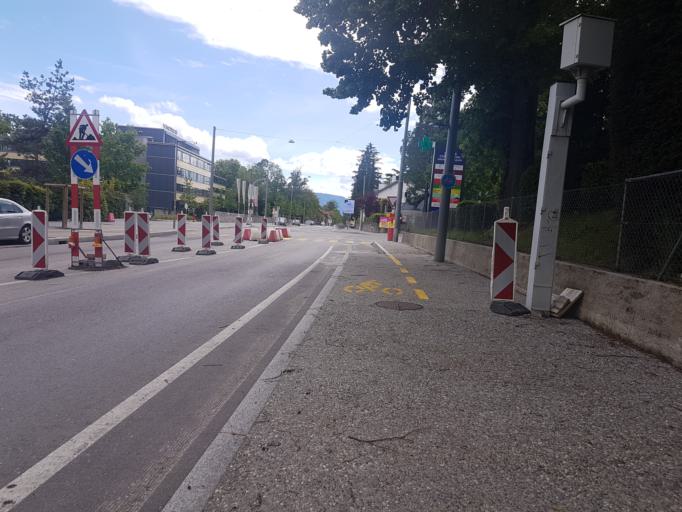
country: CH
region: Geneva
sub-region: Geneva
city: Versoix
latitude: 46.2924
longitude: 6.1656
